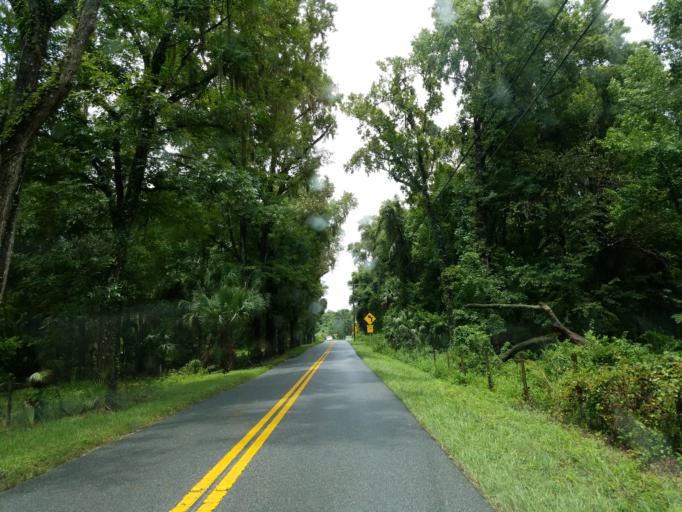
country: US
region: Florida
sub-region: Citrus County
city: Inverness Highlands South
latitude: 28.8086
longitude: -82.2956
